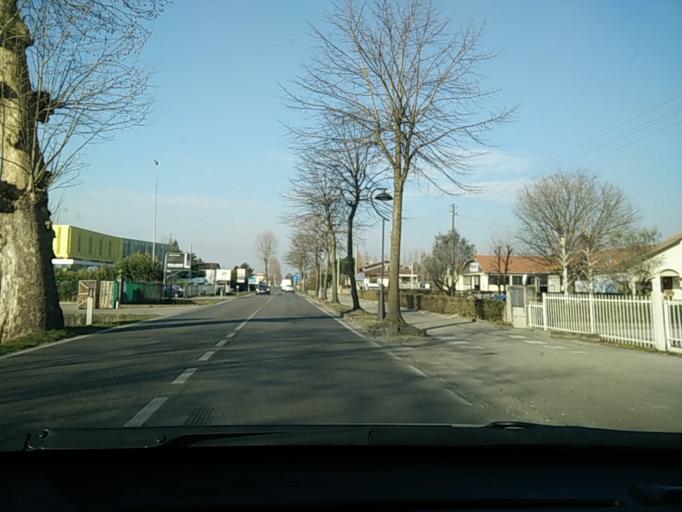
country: IT
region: Veneto
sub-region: Provincia di Treviso
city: San Biagio di Callalta
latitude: 45.6832
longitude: 12.3672
